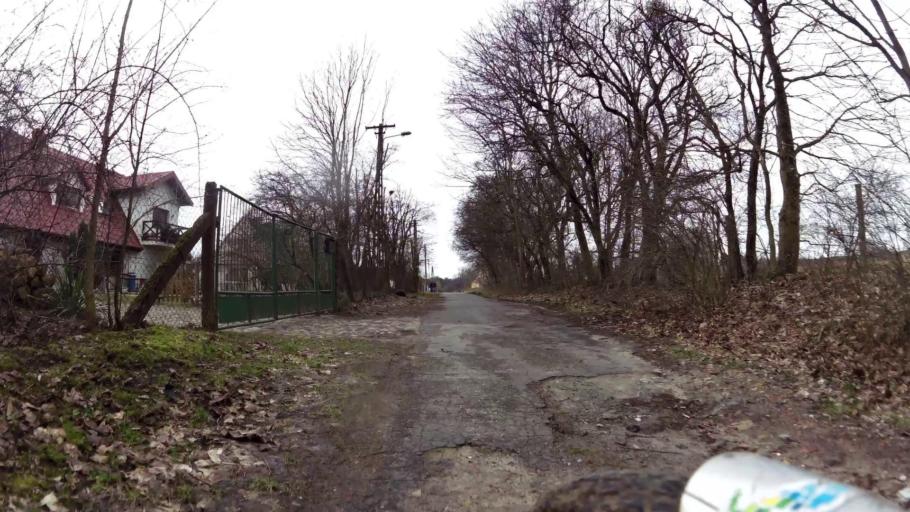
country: PL
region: Pomeranian Voivodeship
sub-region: Powiat bytowski
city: Kolczyglowy
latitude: 54.2403
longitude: 17.2471
